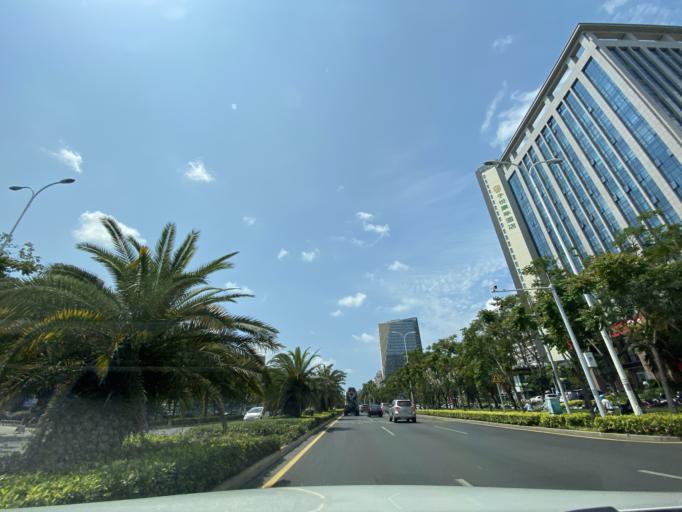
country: CN
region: Hainan
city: Sanya
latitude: 18.2751
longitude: 109.5066
